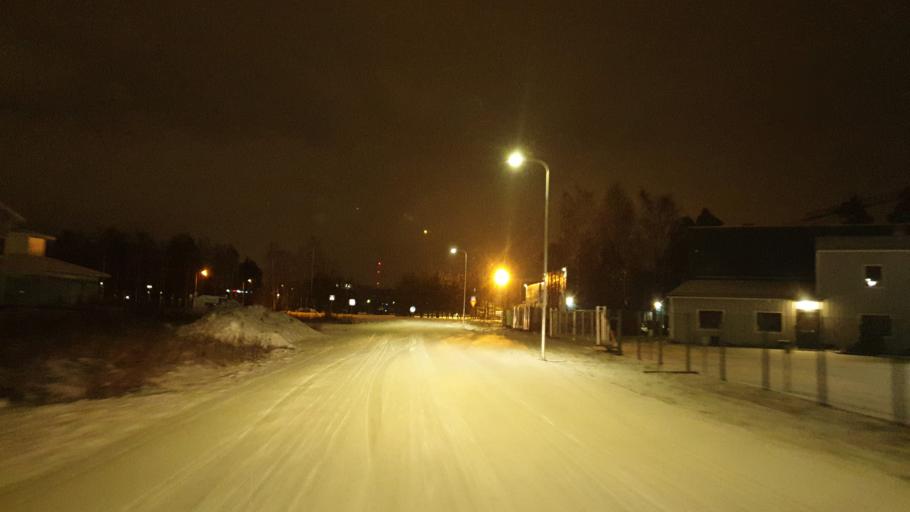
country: FI
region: Northern Ostrobothnia
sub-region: Oulu
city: Oulu
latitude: 64.9941
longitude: 25.4467
